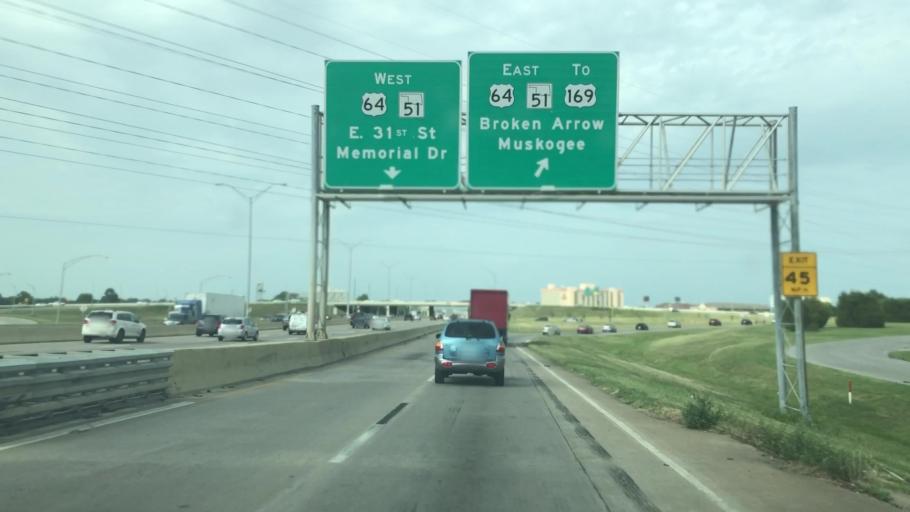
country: US
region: Oklahoma
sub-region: Tulsa County
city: Tulsa
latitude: 36.1112
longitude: -95.8996
